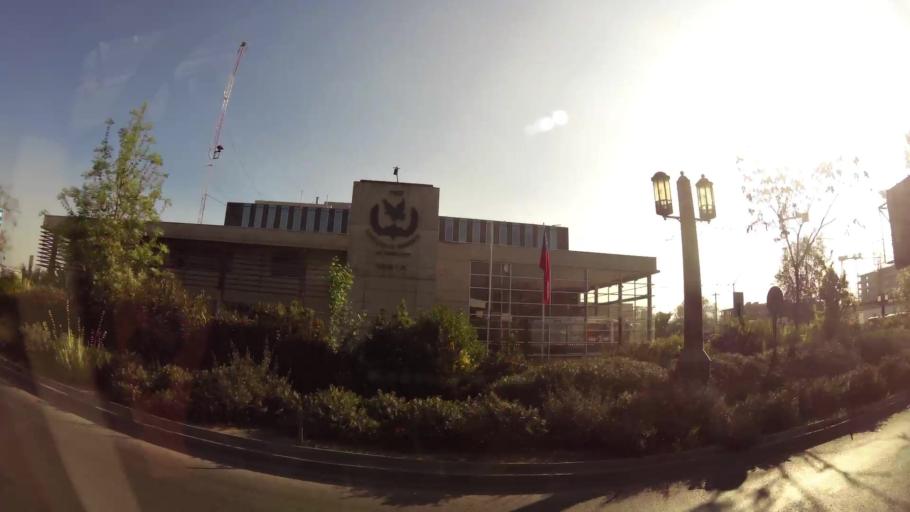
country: CL
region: Santiago Metropolitan
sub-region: Provincia de Santiago
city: Villa Presidente Frei, Nunoa, Santiago, Chile
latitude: -33.3646
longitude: -70.5142
